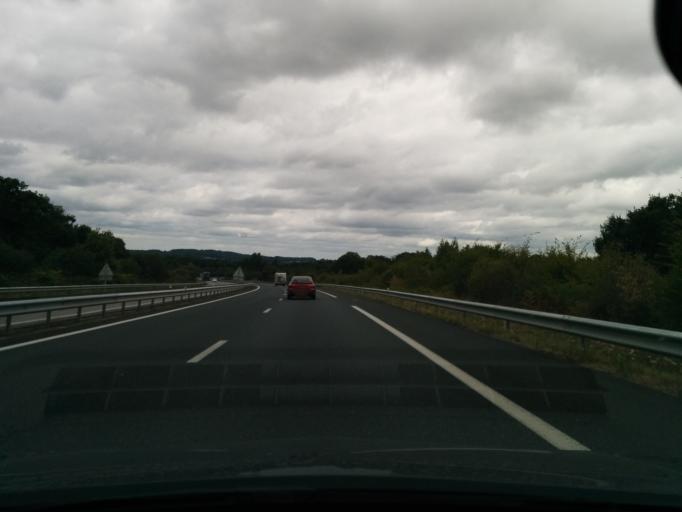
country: FR
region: Limousin
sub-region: Departement de la Haute-Vienne
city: Bessines-sur-Gartempe
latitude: 46.1348
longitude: 1.3807
